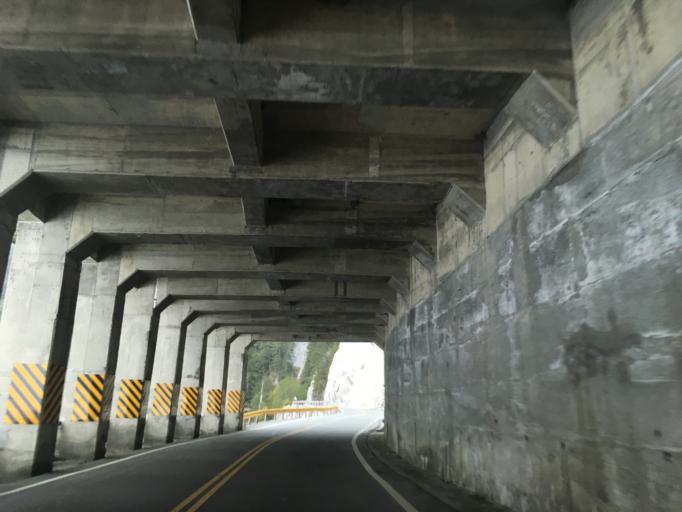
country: TW
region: Taiwan
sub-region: Hualien
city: Hualian
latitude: 24.1748
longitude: 121.3779
